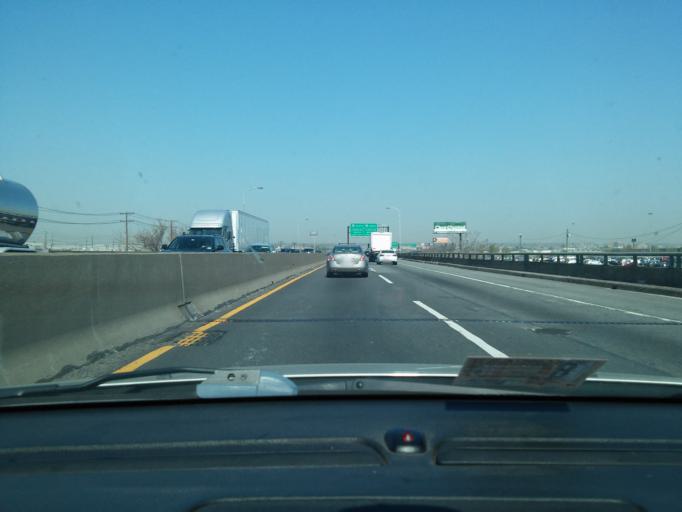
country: US
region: New Jersey
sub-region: Hudson County
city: Bayonne
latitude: 40.7014
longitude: -74.1384
